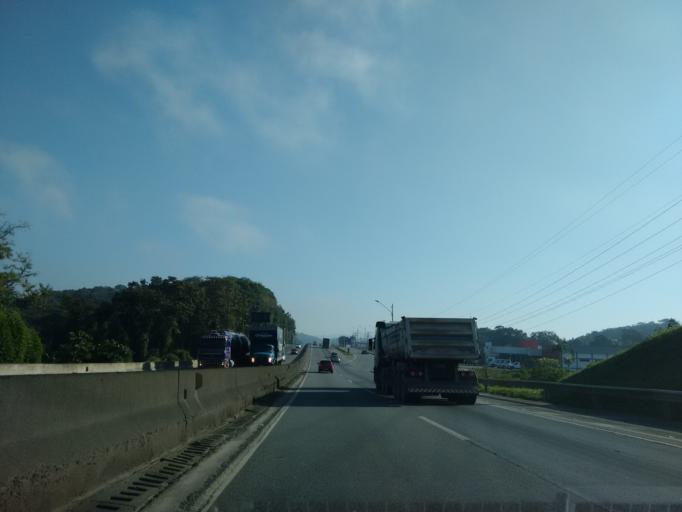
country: BR
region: Santa Catarina
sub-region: Joinville
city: Joinville
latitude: -26.2884
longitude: -48.8858
